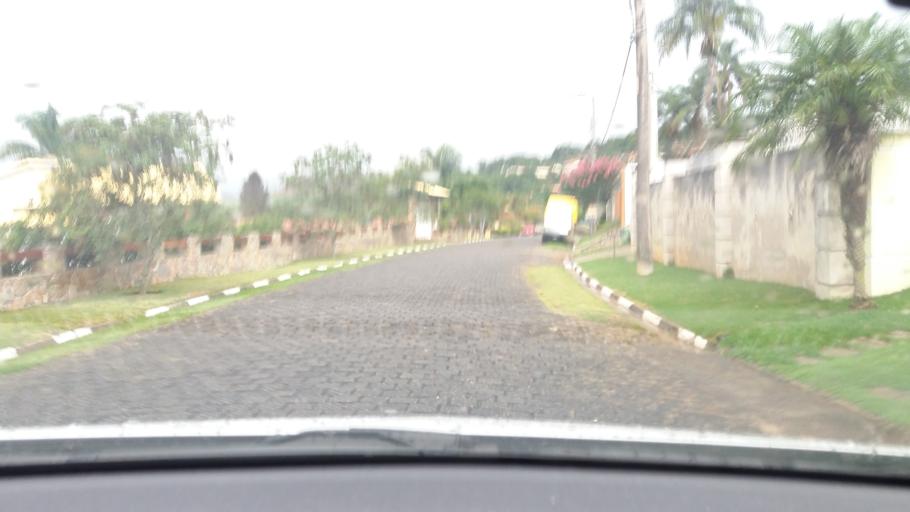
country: BR
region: Sao Paulo
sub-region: Bom Jesus Dos Perdoes
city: Bom Jesus dos Perdoes
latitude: -23.1673
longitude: -46.4529
